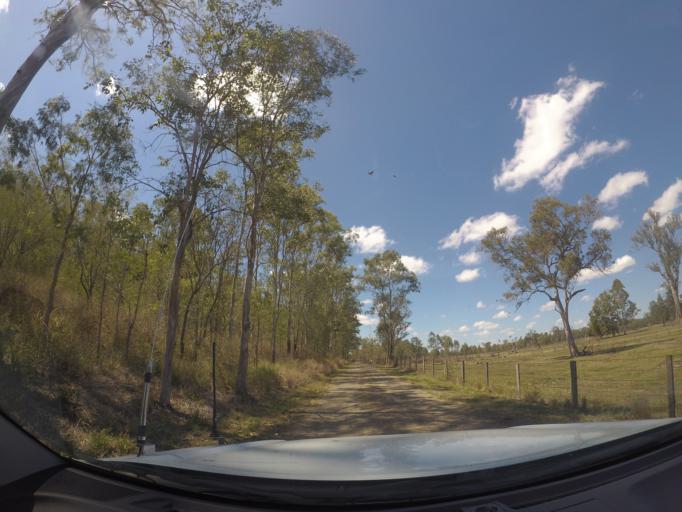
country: AU
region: Queensland
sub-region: Logan
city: Cedar Vale
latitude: -27.8514
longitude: 152.8960
